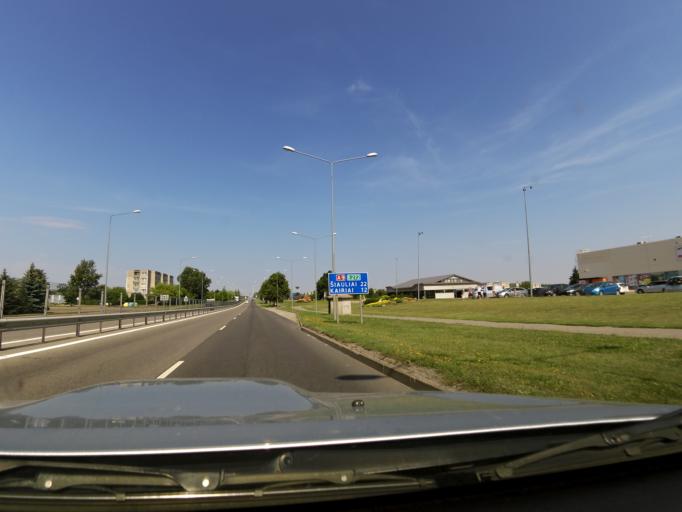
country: LT
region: Siauliu apskritis
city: Radviliskis
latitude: 55.8128
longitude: 23.5468
